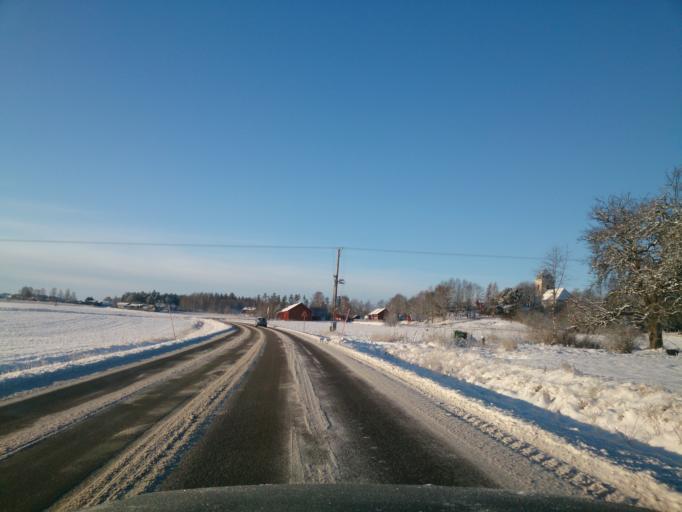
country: SE
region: OEstergoetland
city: Lindo
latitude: 58.5813
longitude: 16.3233
